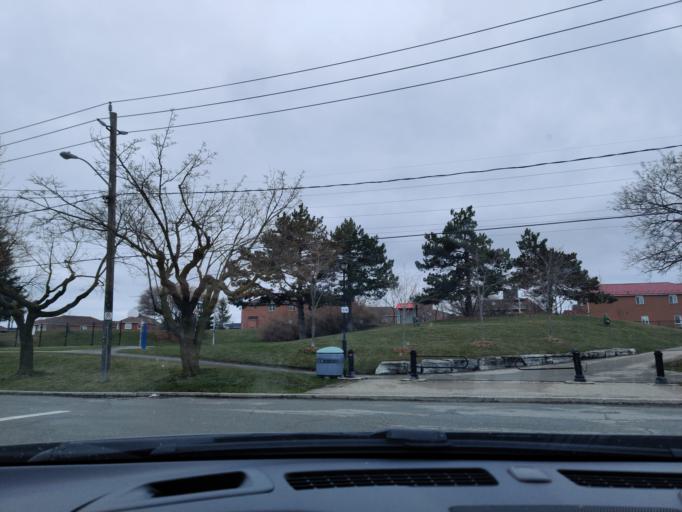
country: CA
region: Ontario
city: Toronto
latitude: 43.6992
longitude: -79.4485
